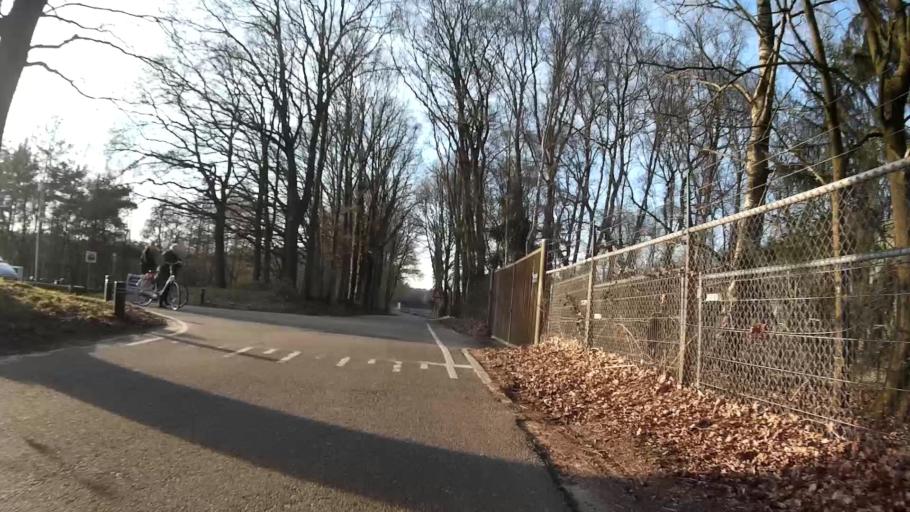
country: NL
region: Utrecht
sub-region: Gemeente Veenendaal
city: Veenendaal
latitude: 51.9940
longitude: 5.5547
